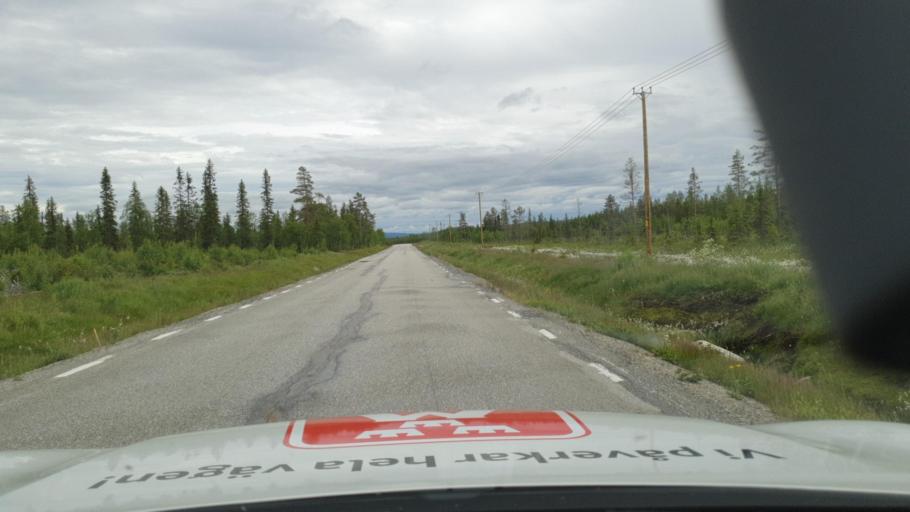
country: SE
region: Vaesterbotten
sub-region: Lycksele Kommun
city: Soderfors
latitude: 64.3843
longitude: 18.0164
